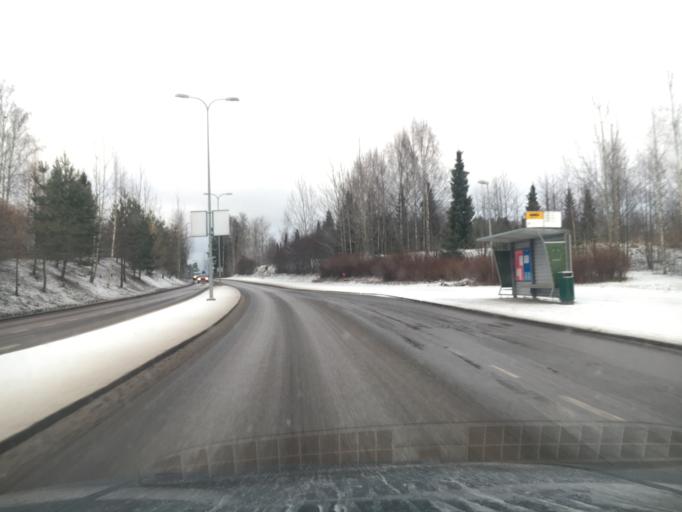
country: FI
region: Uusimaa
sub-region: Helsinki
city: Espoo
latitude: 60.1680
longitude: 24.6609
